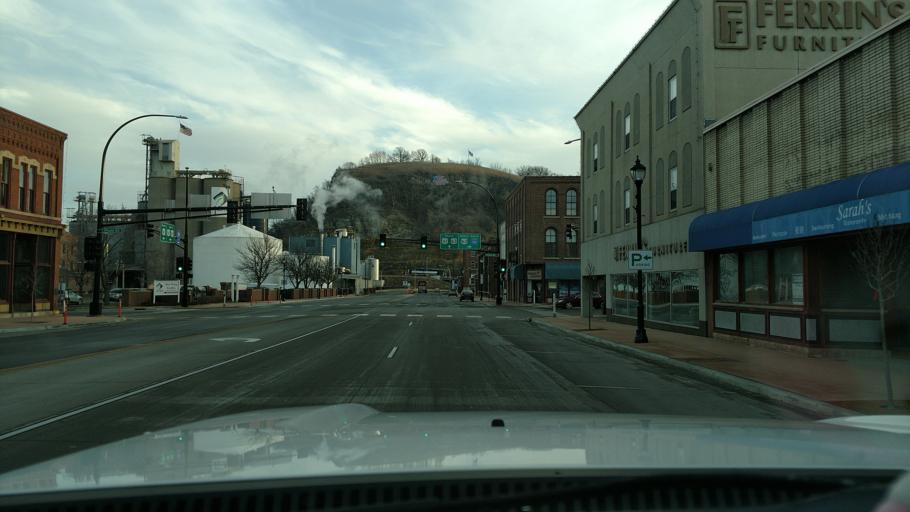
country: US
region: Minnesota
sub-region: Goodhue County
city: Red Wing
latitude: 44.5663
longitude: -92.5346
